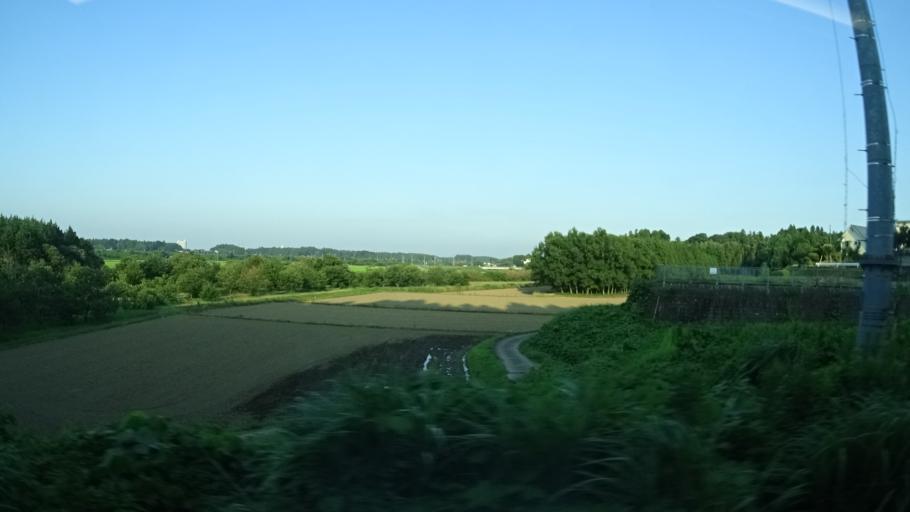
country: JP
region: Ibaraki
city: Tomobe
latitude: 36.3236
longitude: 140.2929
